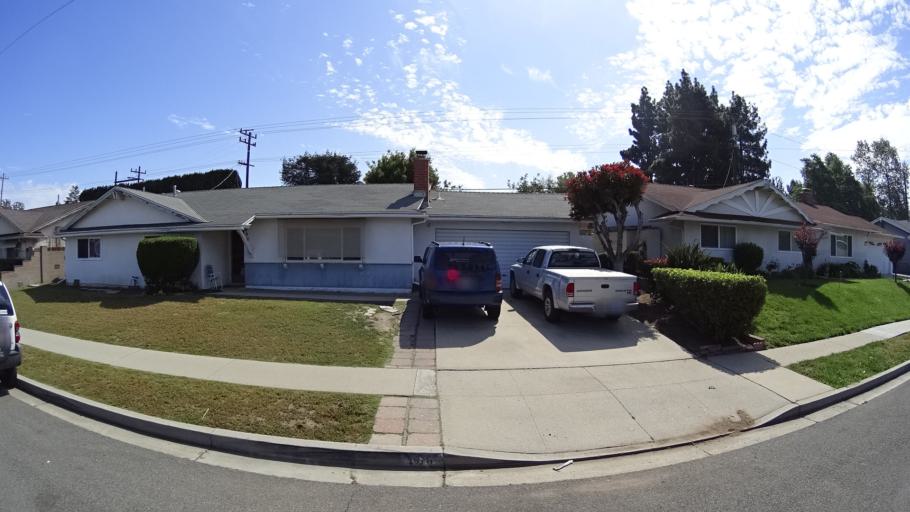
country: US
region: California
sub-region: Ventura County
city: Casa Conejo
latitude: 34.1800
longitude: -118.9391
